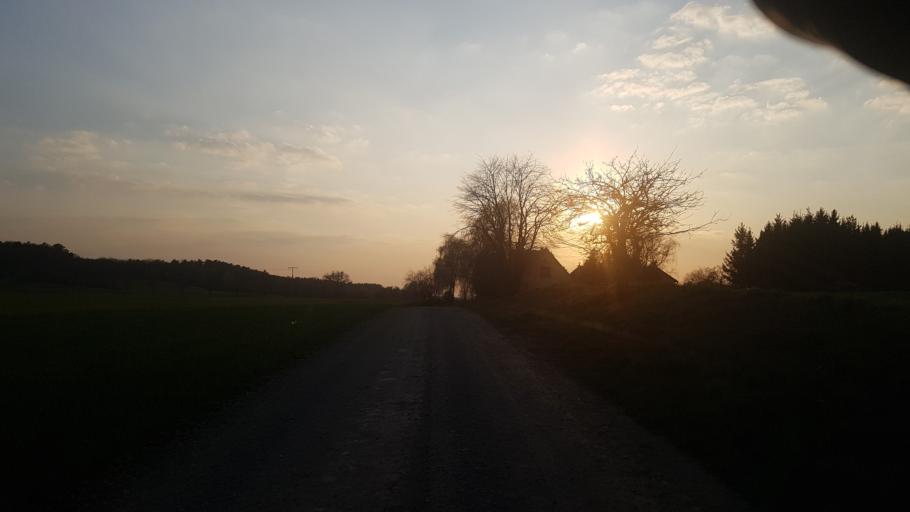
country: DE
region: Brandenburg
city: Gramzow
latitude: 53.2132
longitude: 13.9477
